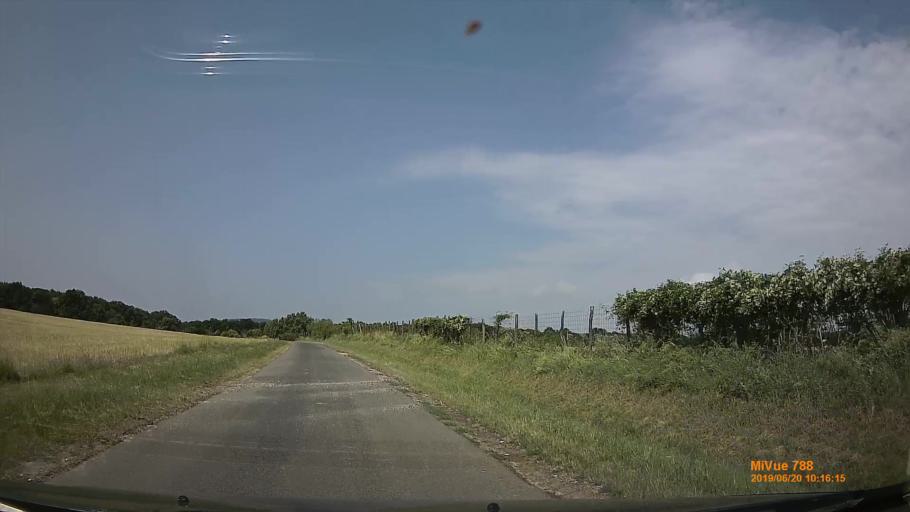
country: HU
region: Baranya
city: Mecseknadasd
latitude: 46.1966
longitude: 18.4589
